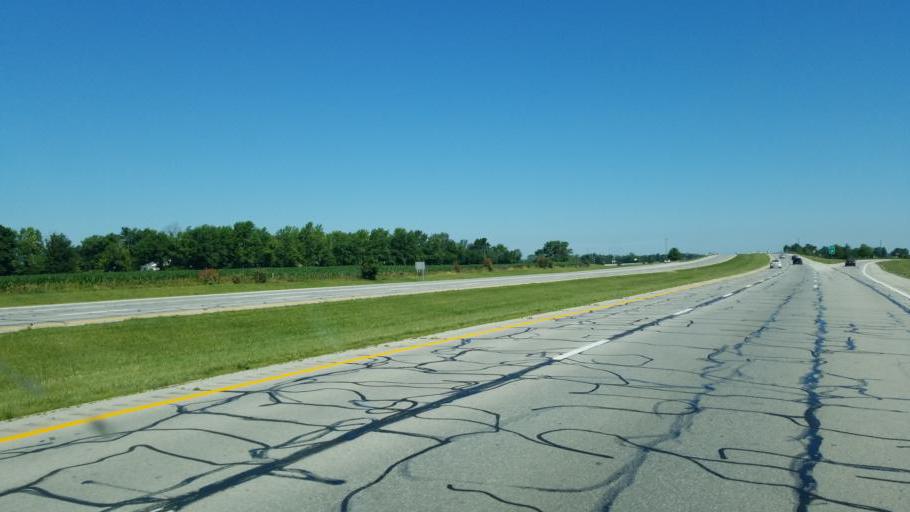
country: US
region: Ohio
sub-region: Marion County
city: Marion
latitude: 40.6600
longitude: -83.1084
